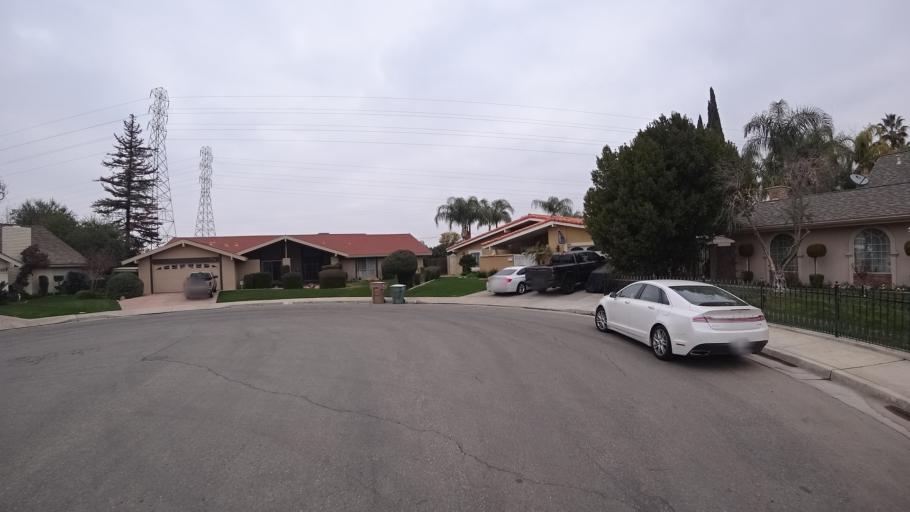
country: US
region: California
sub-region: Kern County
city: Bakersfield
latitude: 35.3847
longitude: -119.0345
